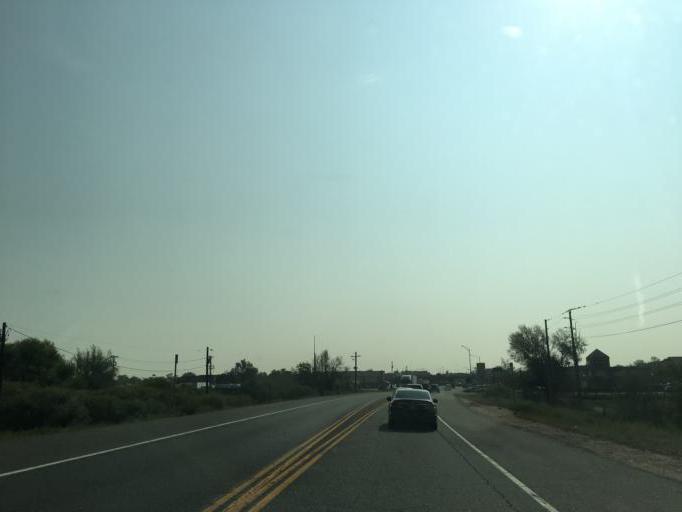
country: US
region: Colorado
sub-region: Adams County
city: Brighton
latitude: 39.9869
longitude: -104.8296
